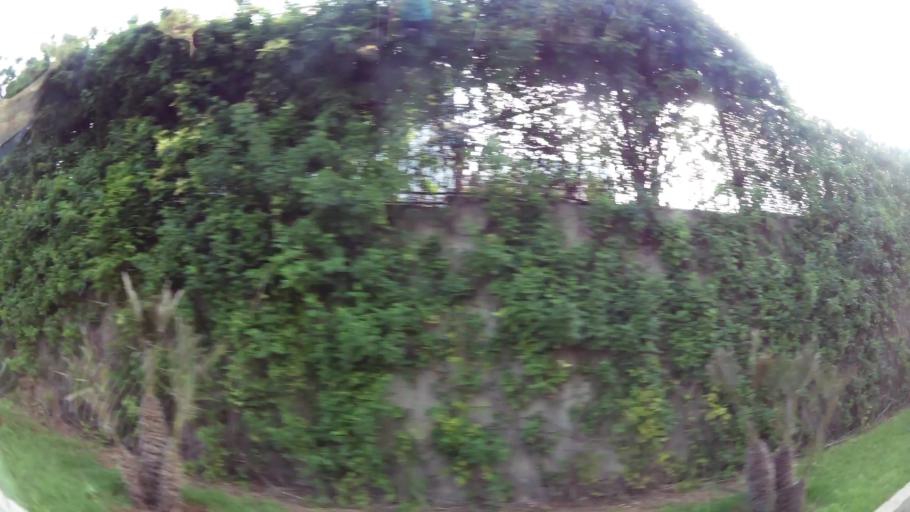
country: MA
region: Rabat-Sale-Zemmour-Zaer
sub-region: Rabat
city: Rabat
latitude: 33.9606
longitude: -6.8390
